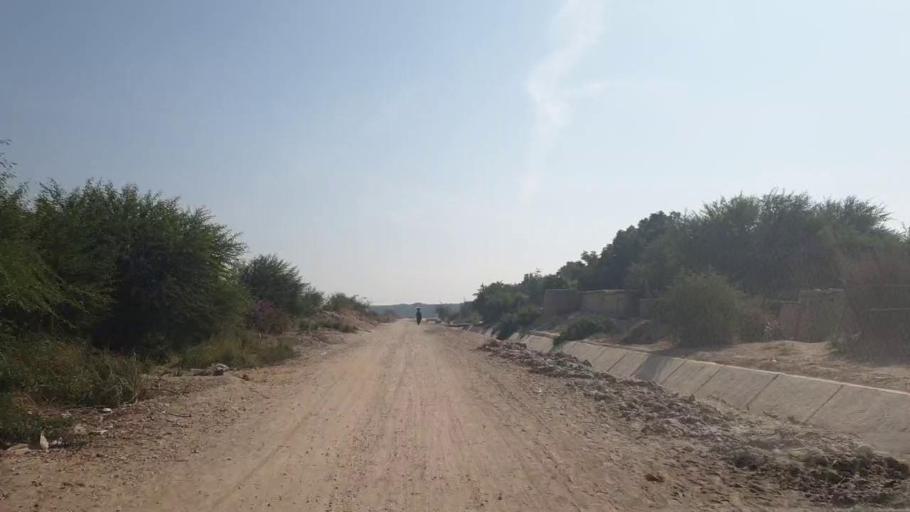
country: PK
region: Sindh
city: Matiari
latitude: 25.6757
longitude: 68.3475
